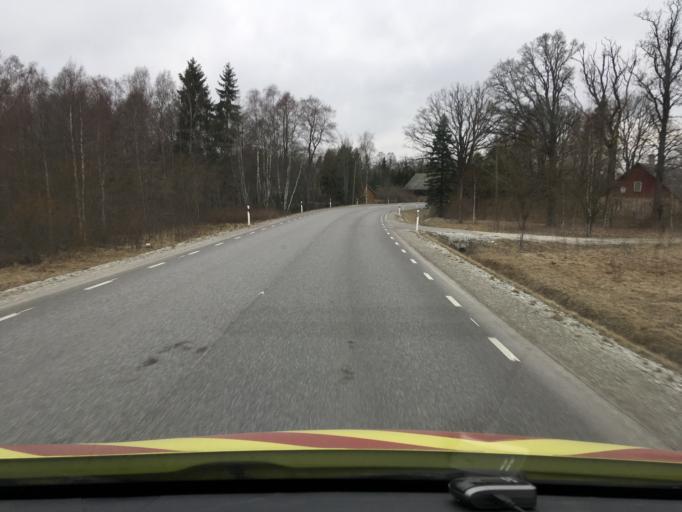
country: EE
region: Raplamaa
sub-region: Rapla vald
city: Rapla
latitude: 58.9985
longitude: 24.8438
